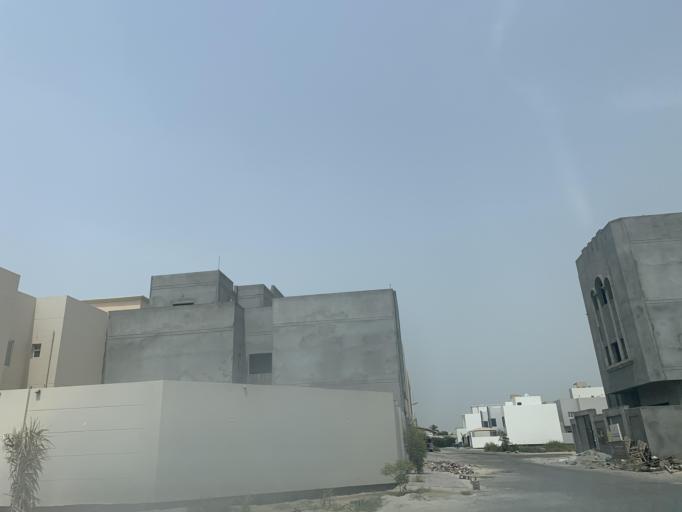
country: BH
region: Manama
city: Jidd Hafs
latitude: 26.1992
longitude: 50.4666
